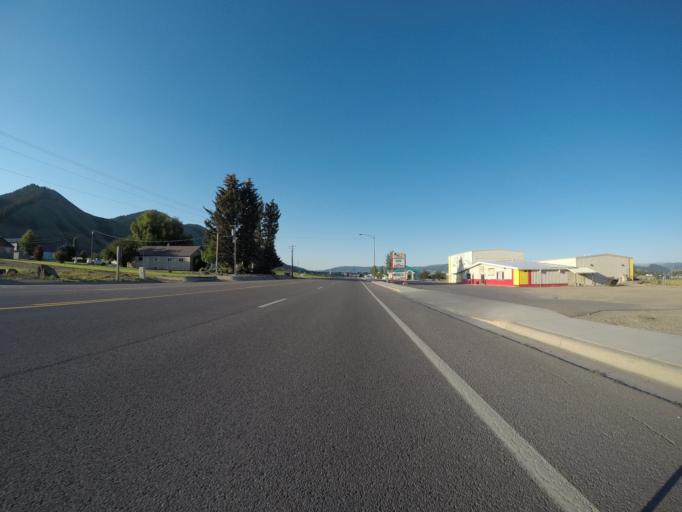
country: US
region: Wyoming
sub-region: Lincoln County
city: Afton
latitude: 42.7142
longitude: -110.9336
